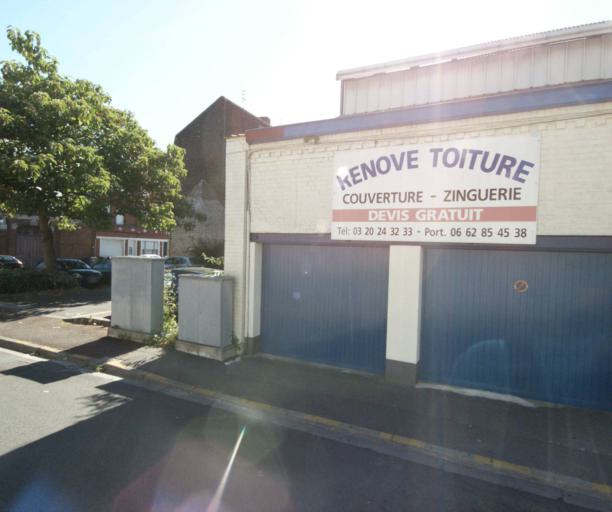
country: FR
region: Nord-Pas-de-Calais
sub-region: Departement du Nord
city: Tourcoing
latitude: 50.7207
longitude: 3.1699
